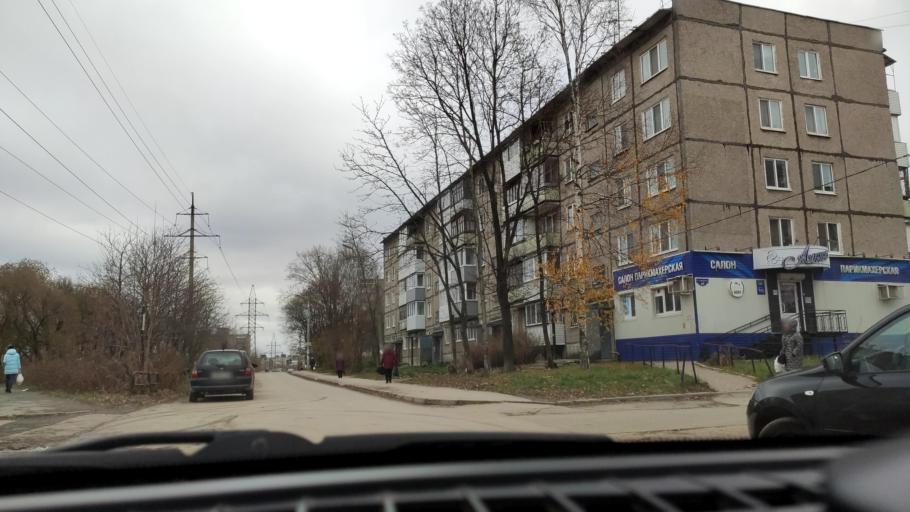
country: RU
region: Perm
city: Perm
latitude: 57.9798
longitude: 56.2169
